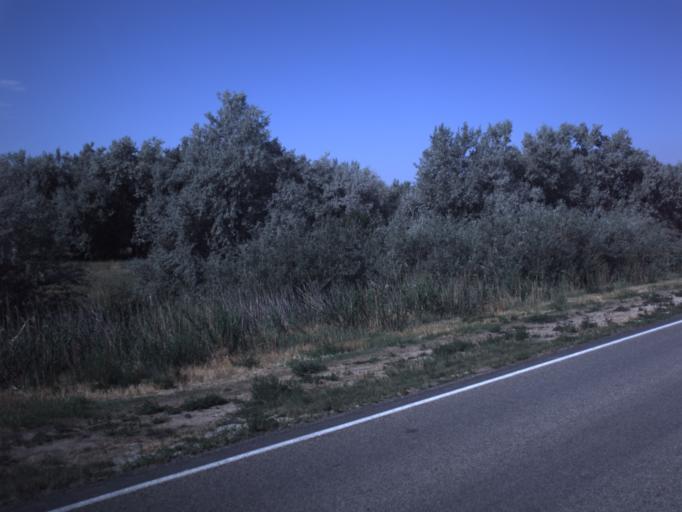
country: US
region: Utah
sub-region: Sanpete County
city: Mount Pleasant
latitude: 39.5467
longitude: -111.5175
